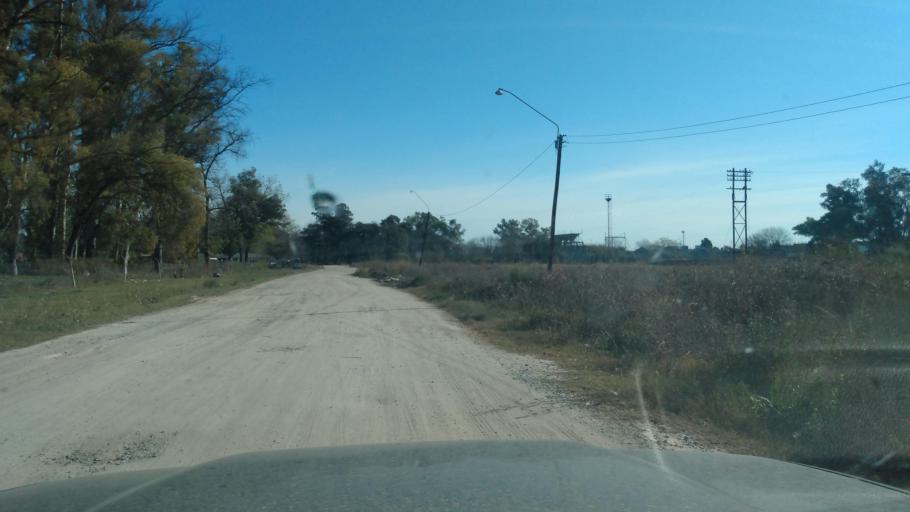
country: AR
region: Buenos Aires
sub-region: Partido de Lujan
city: Lujan
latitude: -34.5766
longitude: -59.0923
